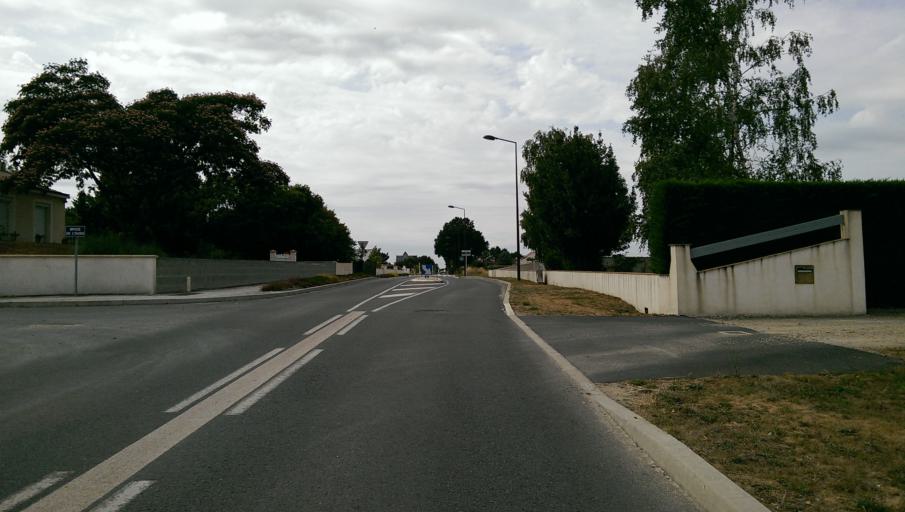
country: FR
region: Pays de la Loire
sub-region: Departement de la Loire-Atlantique
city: La Planche
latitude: 47.0114
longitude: -1.4275
